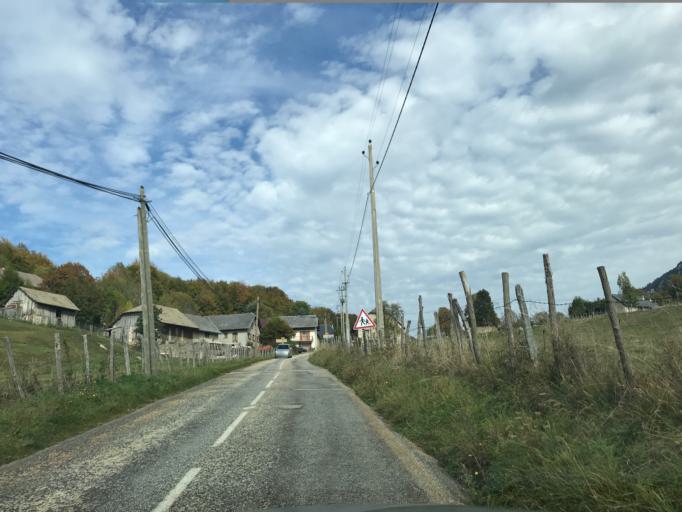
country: FR
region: Rhone-Alpes
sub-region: Departement de la Savoie
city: Les Echelles
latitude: 45.4405
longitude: 5.8101
